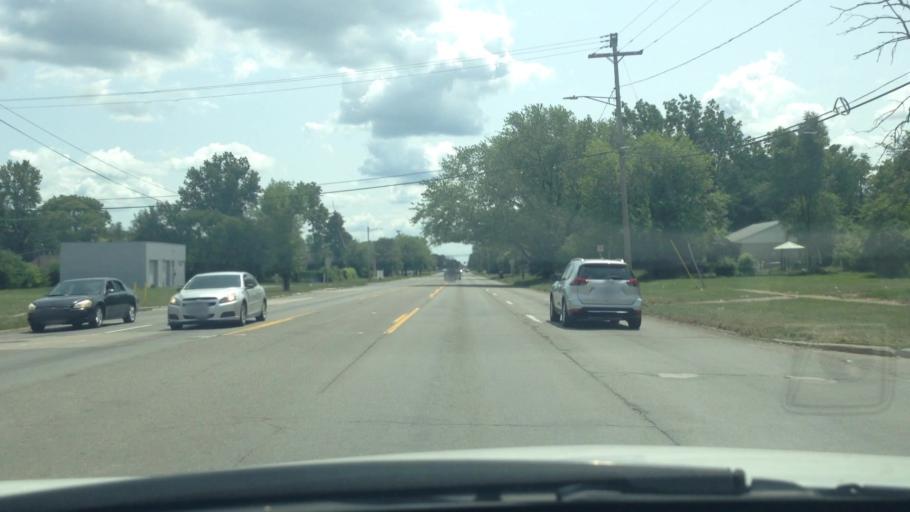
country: US
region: Michigan
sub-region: Wayne County
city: Inkster
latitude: 42.2876
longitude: -83.3098
